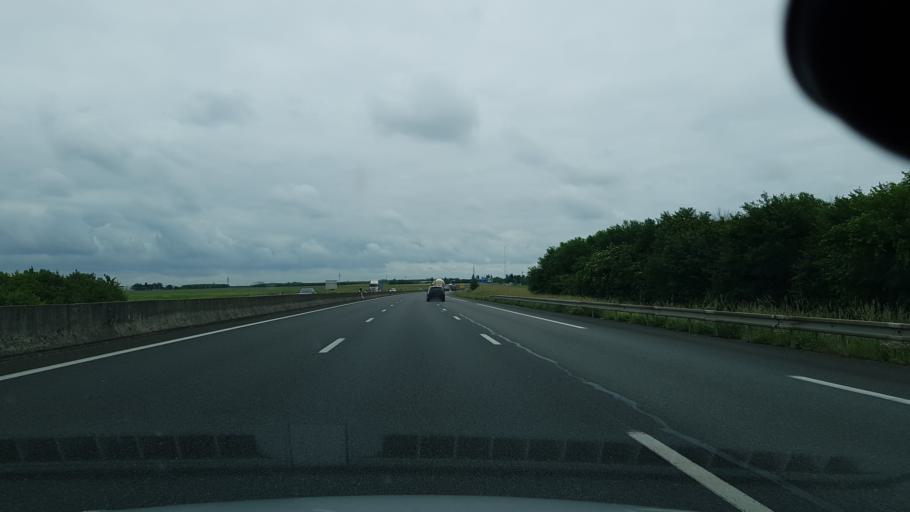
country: FR
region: Centre
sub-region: Departement du Loir-et-Cher
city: La Chaussee-Saint-Victor
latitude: 47.6331
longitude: 1.3551
